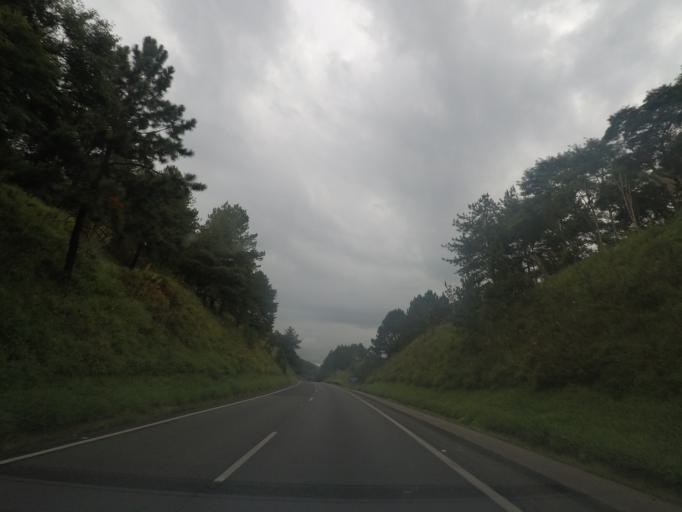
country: BR
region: Parana
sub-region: Campina Grande Do Sul
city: Campina Grande do Sul
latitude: -25.1119
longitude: -48.8534
